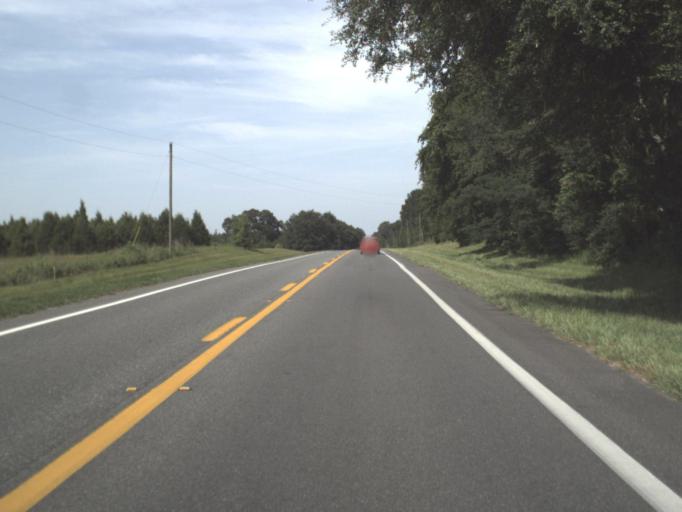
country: US
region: Florida
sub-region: Suwannee County
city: Live Oak
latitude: 30.2295
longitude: -83.0666
